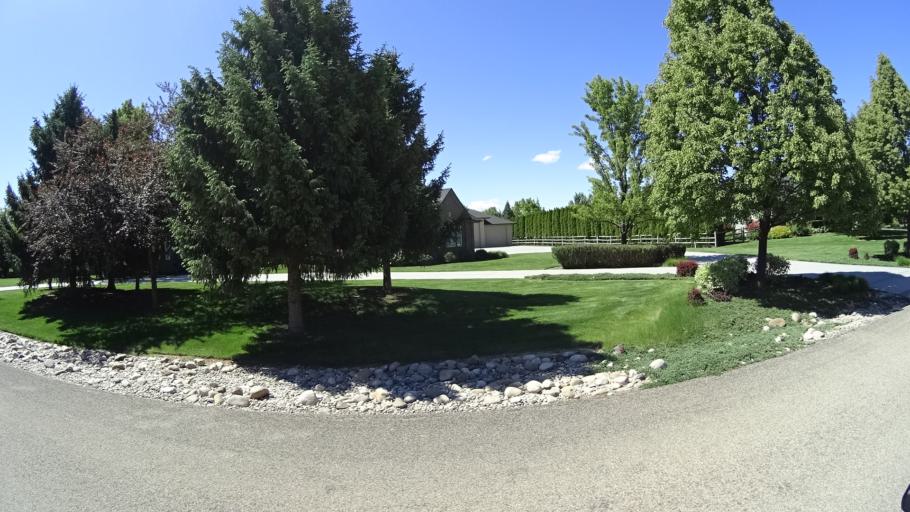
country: US
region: Idaho
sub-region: Ada County
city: Eagle
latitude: 43.6674
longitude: -116.3872
